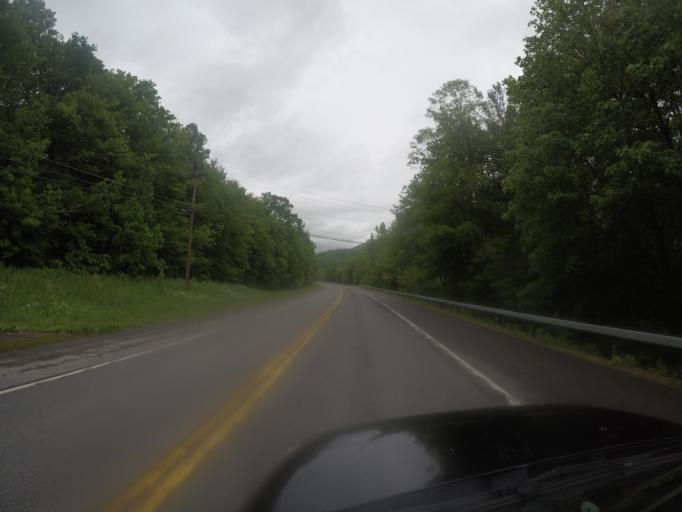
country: US
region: New York
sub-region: Ulster County
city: Shokan
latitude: 42.0752
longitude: -74.3070
